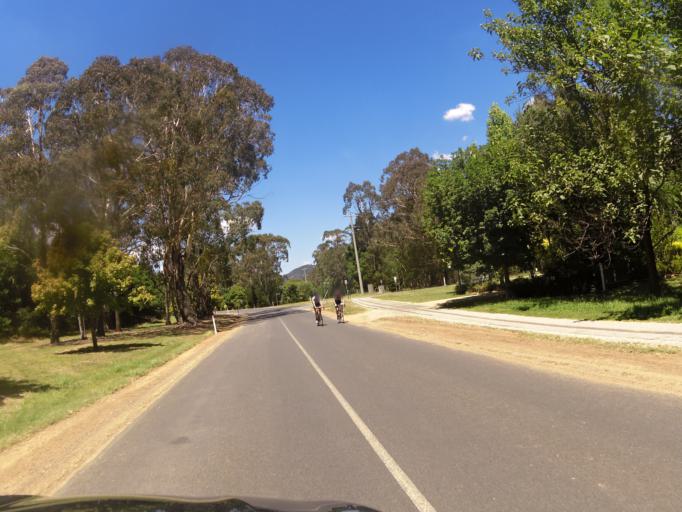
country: AU
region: Victoria
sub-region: Alpine
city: Mount Beauty
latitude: -36.7153
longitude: 146.9423
